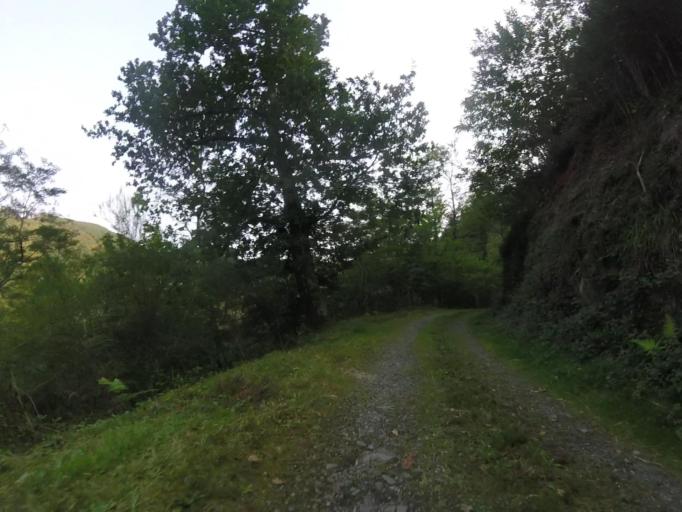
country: ES
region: Navarre
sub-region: Provincia de Navarra
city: Arano
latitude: 43.2584
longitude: -1.8489
